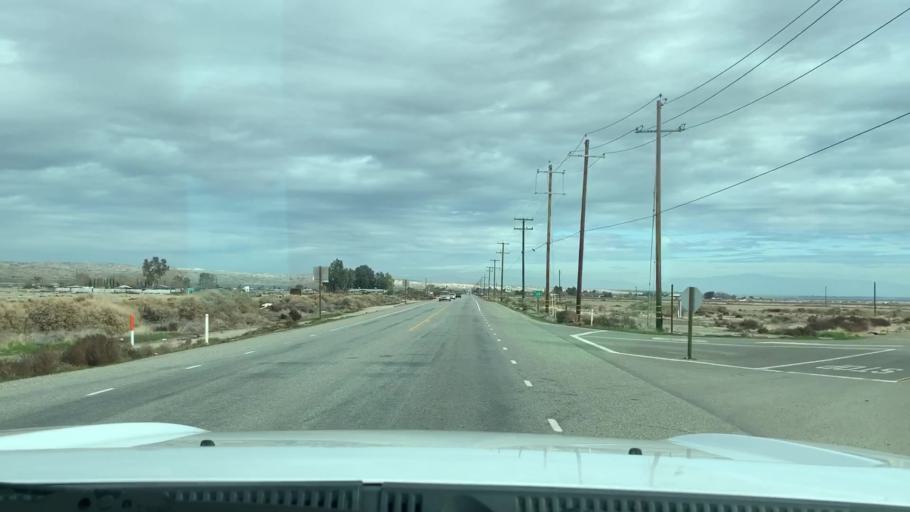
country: US
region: California
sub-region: Kern County
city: Ford City
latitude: 35.2098
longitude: -119.4049
